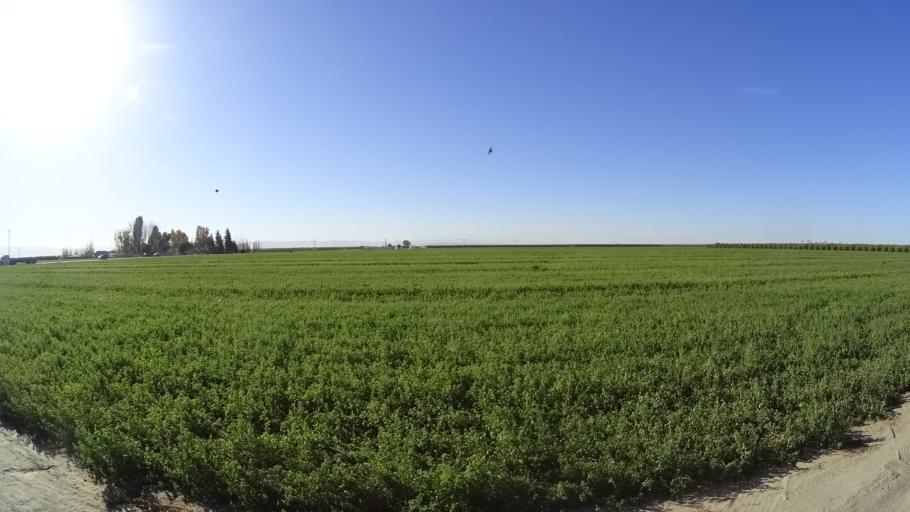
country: US
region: California
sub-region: Kern County
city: Greenacres
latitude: 35.2684
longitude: -119.1183
